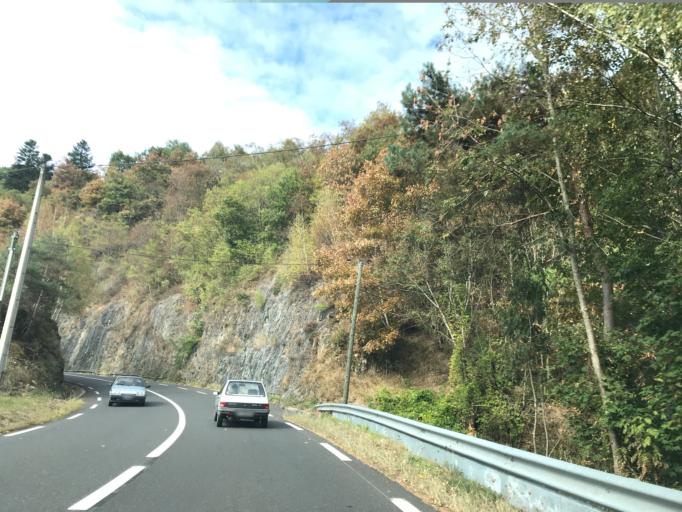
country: FR
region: Auvergne
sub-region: Departement du Puy-de-Dome
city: Thiers
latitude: 45.8661
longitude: 3.5678
